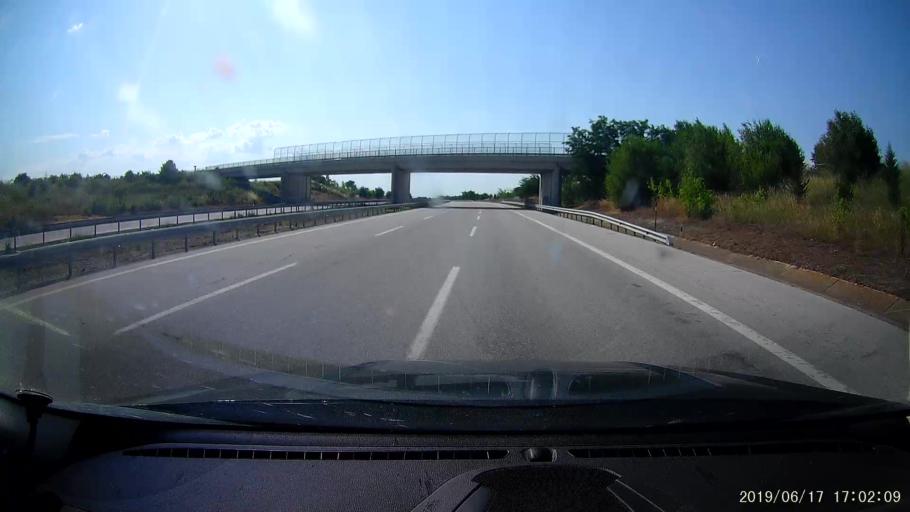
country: TR
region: Edirne
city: Haskoy
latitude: 41.6368
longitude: 26.7881
